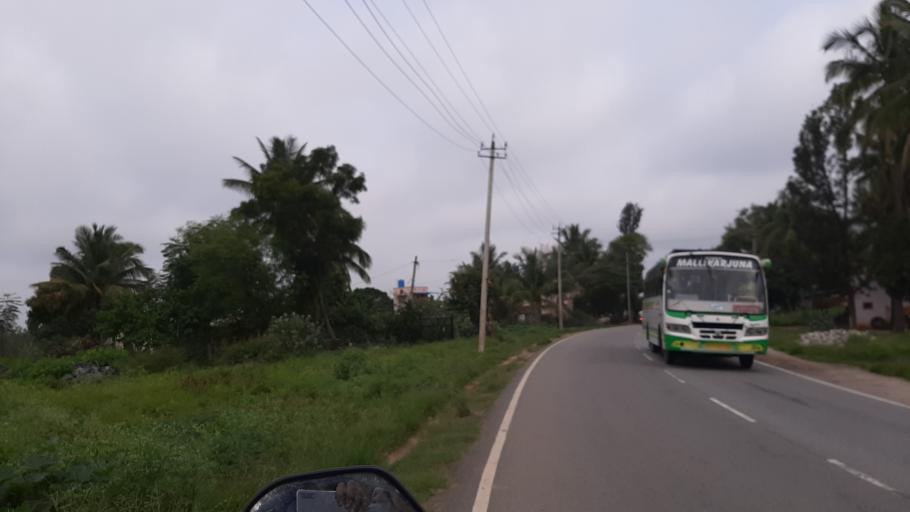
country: IN
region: Karnataka
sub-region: Bangalore Rural
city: Nelamangala
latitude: 12.9670
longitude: 77.3789
